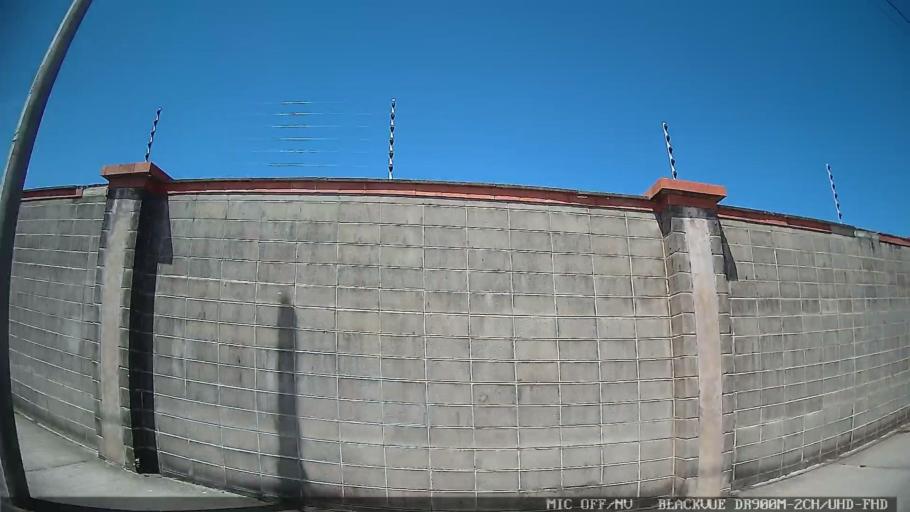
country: BR
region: Sao Paulo
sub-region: Peruibe
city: Peruibe
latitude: -24.3011
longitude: -46.9961
